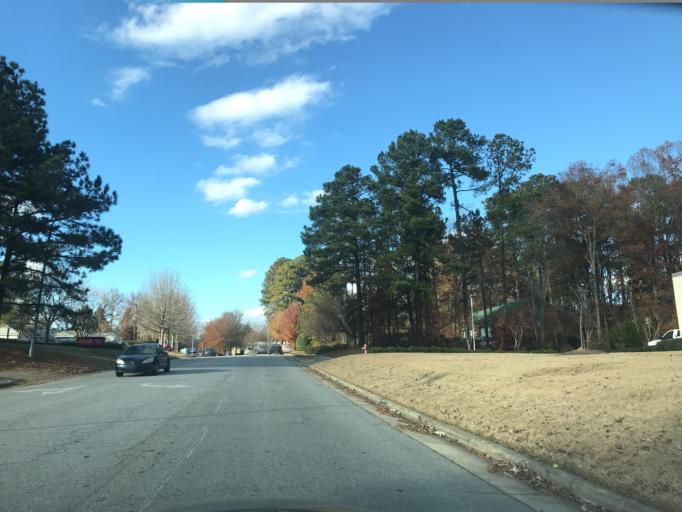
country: US
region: North Carolina
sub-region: Wake County
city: Raleigh
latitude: 35.8488
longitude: -78.5903
